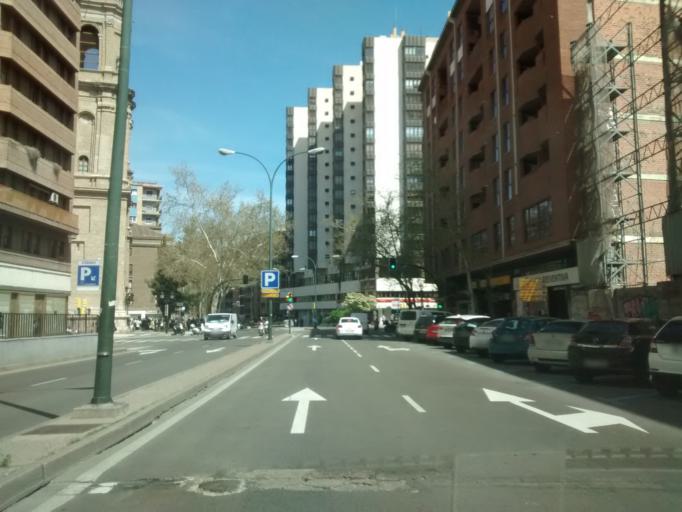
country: ES
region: Aragon
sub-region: Provincia de Zaragoza
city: Zaragoza
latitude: 41.6518
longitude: -0.8855
